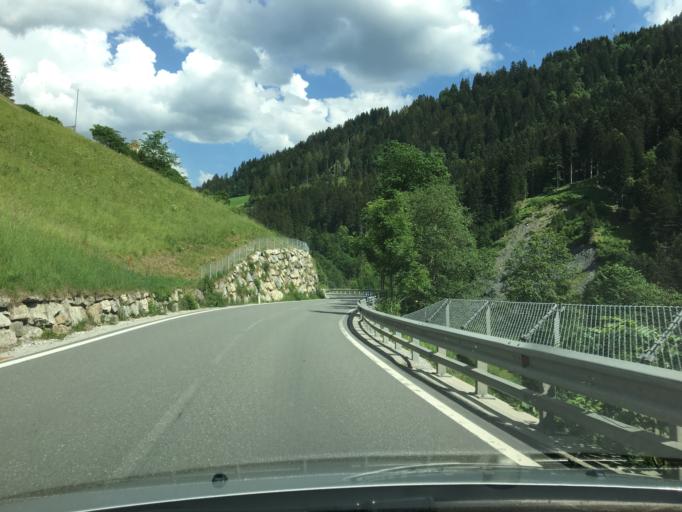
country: AT
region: Salzburg
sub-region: Politischer Bezirk Sankt Johann im Pongau
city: Sankt Johann im Pongau
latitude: 47.3310
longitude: 13.2306
